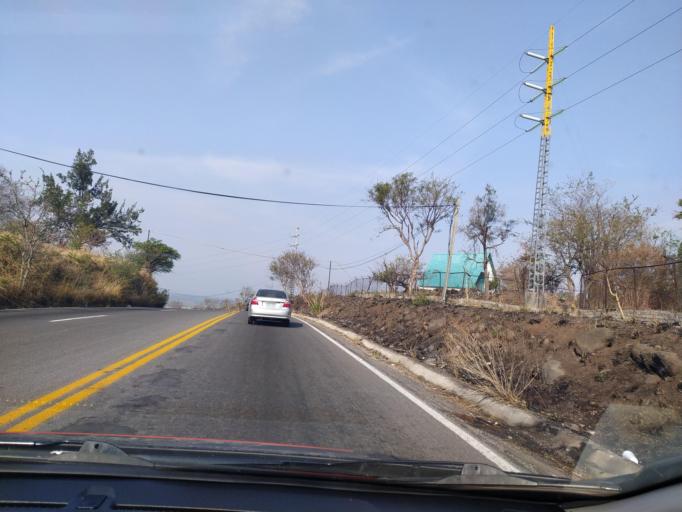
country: MX
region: Jalisco
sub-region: Acatlan de Juarez
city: Villa de los Ninos
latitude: 20.4262
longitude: -103.5820
